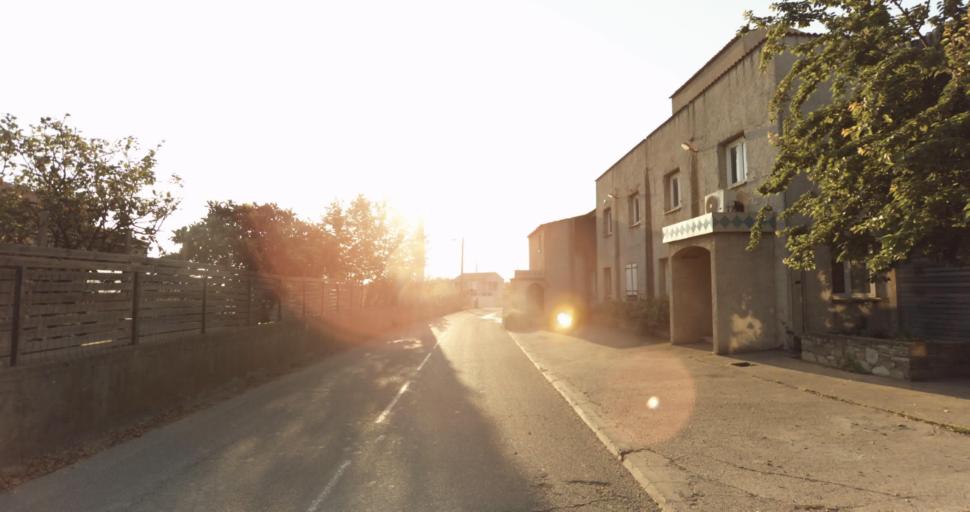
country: FR
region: Corsica
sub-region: Departement de la Haute-Corse
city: Biguglia
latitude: 42.6289
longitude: 9.4401
